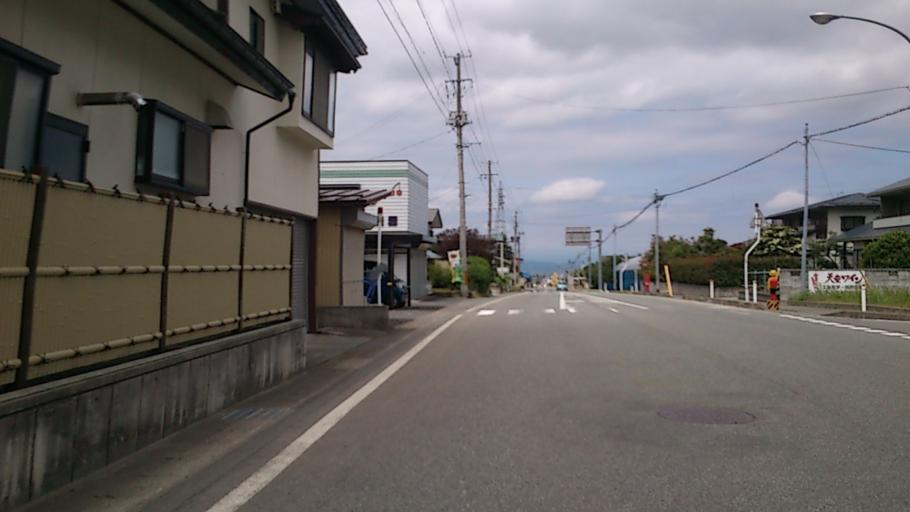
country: JP
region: Yamagata
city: Tendo
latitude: 38.3120
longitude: 140.4166
